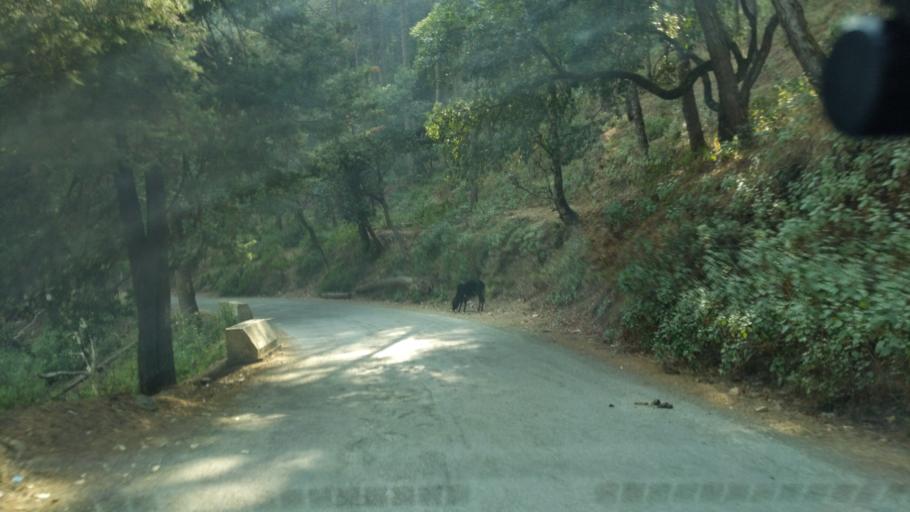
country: IN
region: Uttarakhand
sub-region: Naini Tal
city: Bhowali
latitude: 29.3970
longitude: 79.5381
